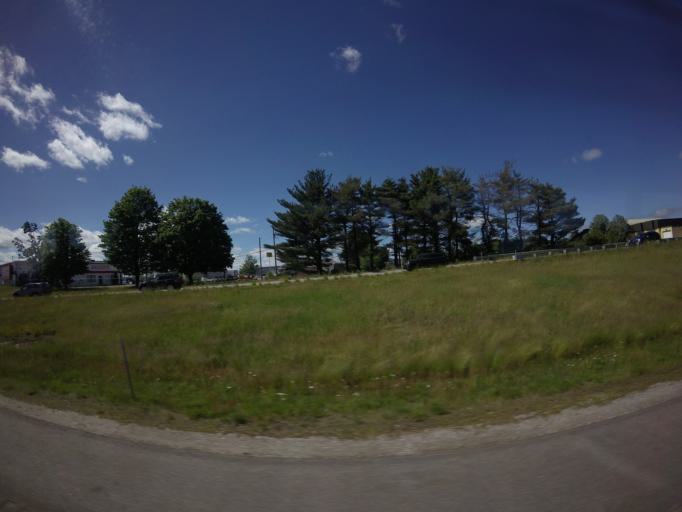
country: US
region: New Hampshire
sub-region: Hillsborough County
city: Manchester
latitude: 42.9567
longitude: -71.4376
